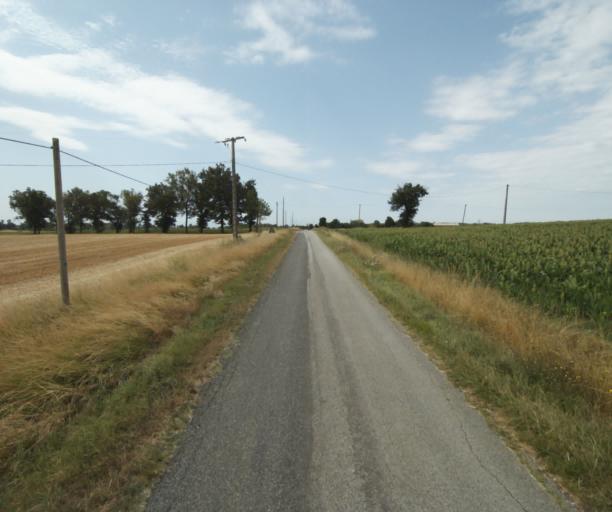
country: FR
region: Midi-Pyrenees
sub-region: Departement de la Haute-Garonne
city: Saint-Felix-Lauragais
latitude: 43.4349
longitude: 1.9041
